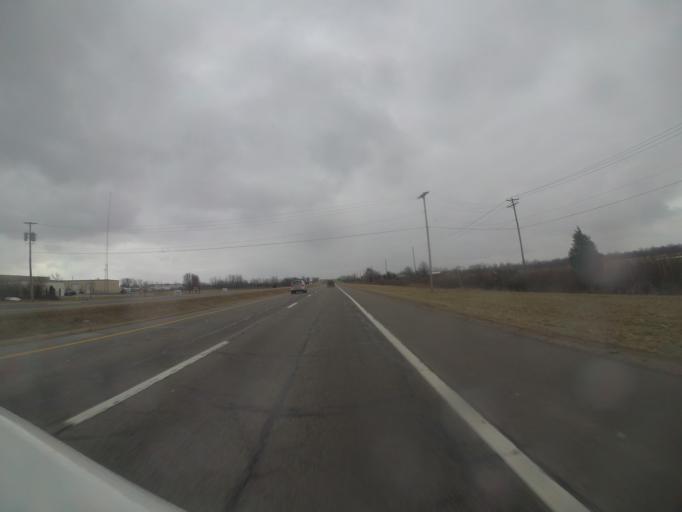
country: US
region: Ohio
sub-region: Wood County
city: Walbridge
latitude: 41.5636
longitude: -83.5242
